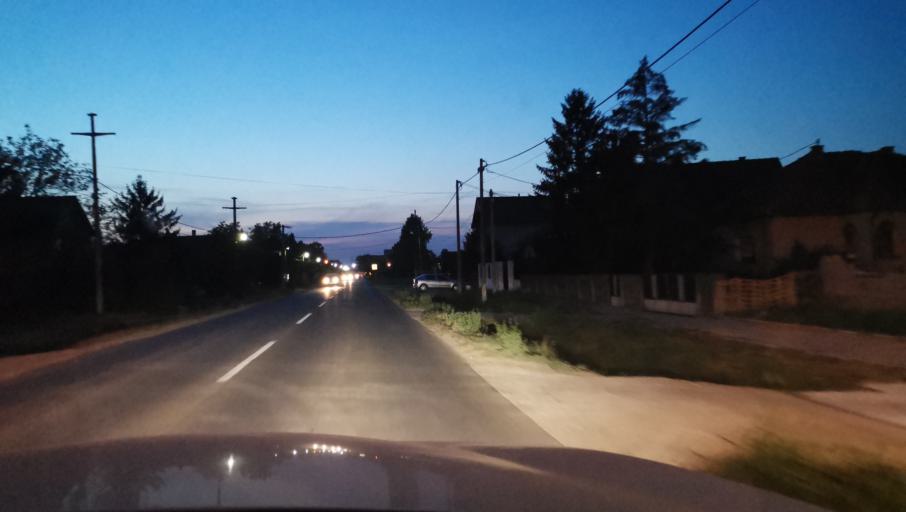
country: RS
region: Central Serbia
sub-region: Belgrade
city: Surcin
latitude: 44.7611
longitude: 20.2531
